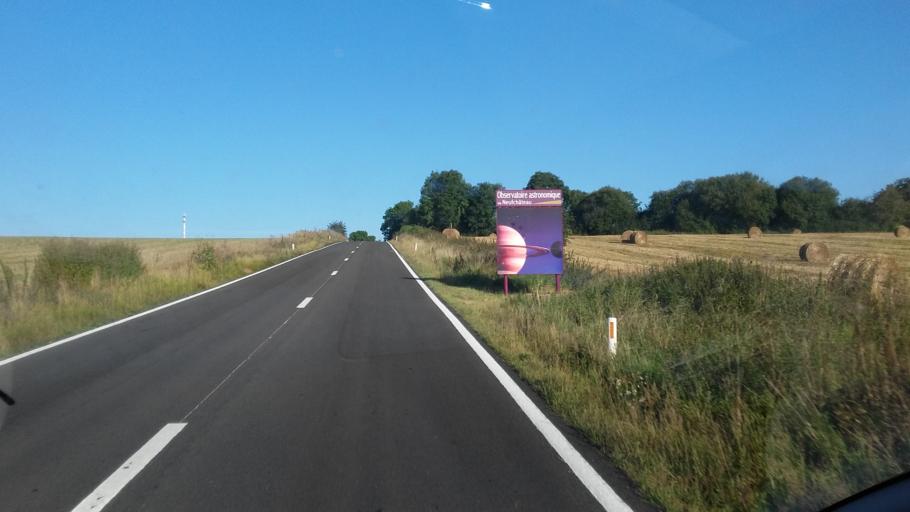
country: BE
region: Wallonia
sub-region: Province du Luxembourg
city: Leglise
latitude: 49.8235
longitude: 5.4904
